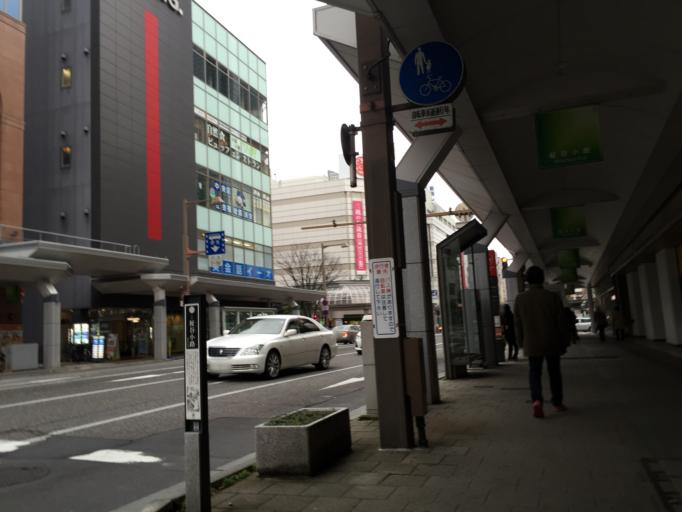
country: JP
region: Niigata
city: Niigata-shi
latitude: 37.9218
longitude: 139.0446
